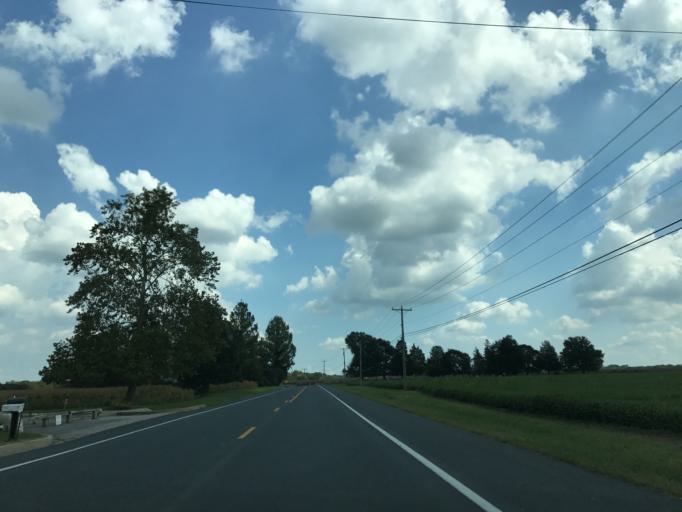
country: US
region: Maryland
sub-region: Caroline County
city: Greensboro
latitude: 39.1344
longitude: -75.7779
